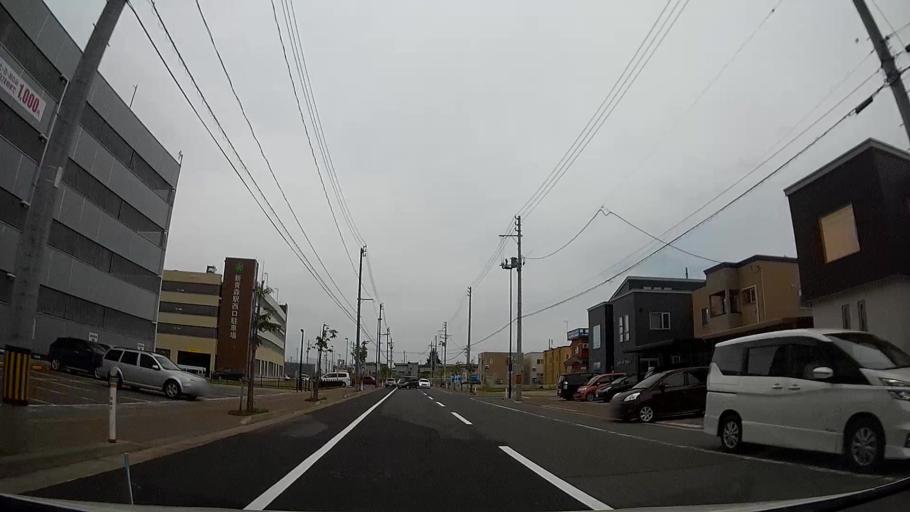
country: JP
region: Aomori
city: Aomori Shi
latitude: 40.8295
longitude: 140.6922
